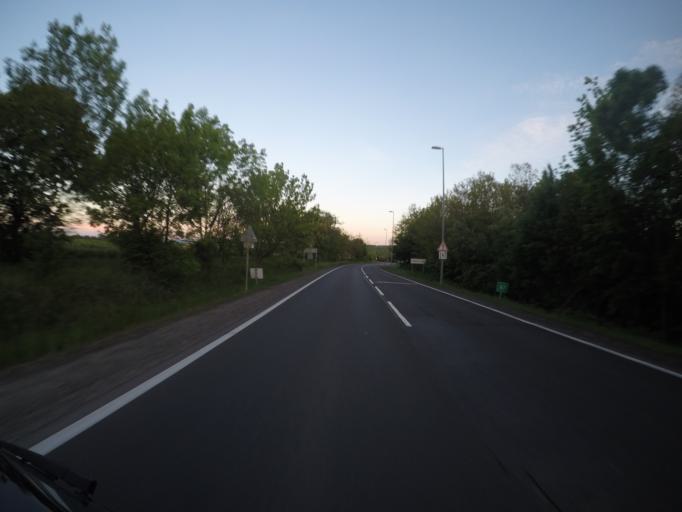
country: HU
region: Nograd
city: Nagyoroszi
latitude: 48.0106
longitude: 19.0783
